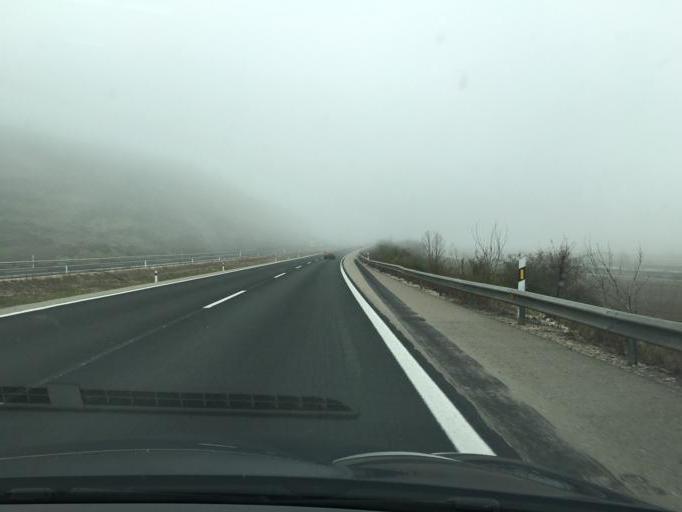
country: ES
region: Castille and Leon
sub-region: Provincia de Burgos
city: Pancorbo
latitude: 42.6218
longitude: -3.1267
